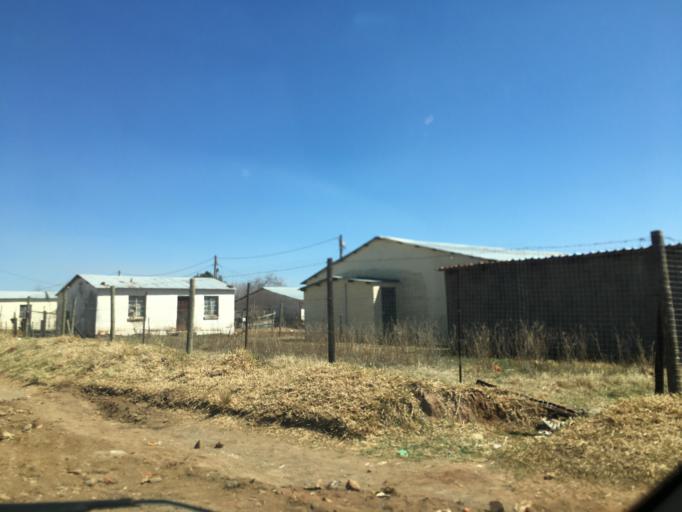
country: ZA
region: Eastern Cape
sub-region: Chris Hani District Municipality
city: Elliot
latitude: -31.3287
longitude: 27.8238
